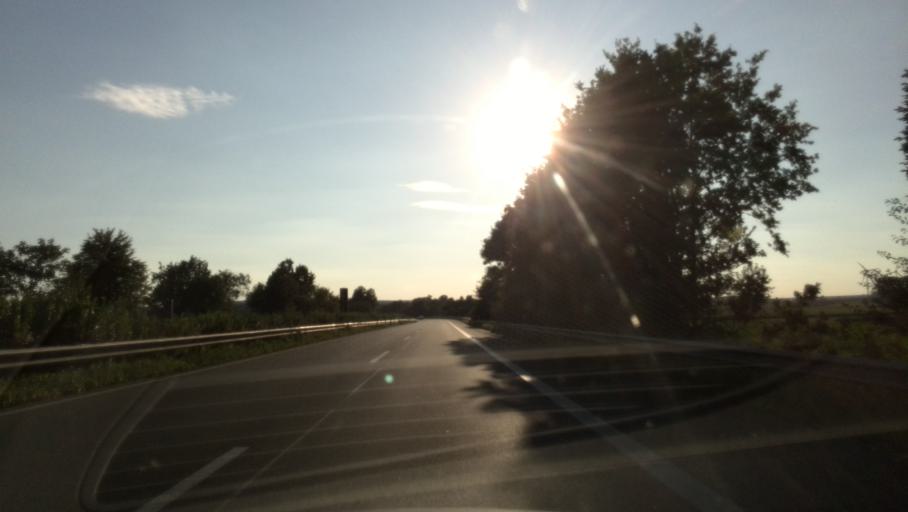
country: DE
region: Lower Saxony
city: Burgdorf
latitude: 52.1373
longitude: 10.2674
